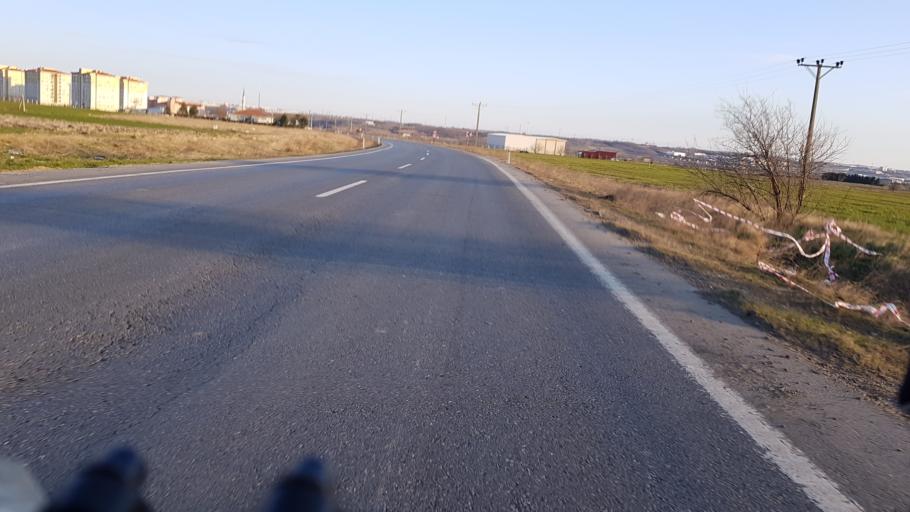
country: TR
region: Tekirdag
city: Velimese
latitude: 41.2562
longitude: 27.8615
